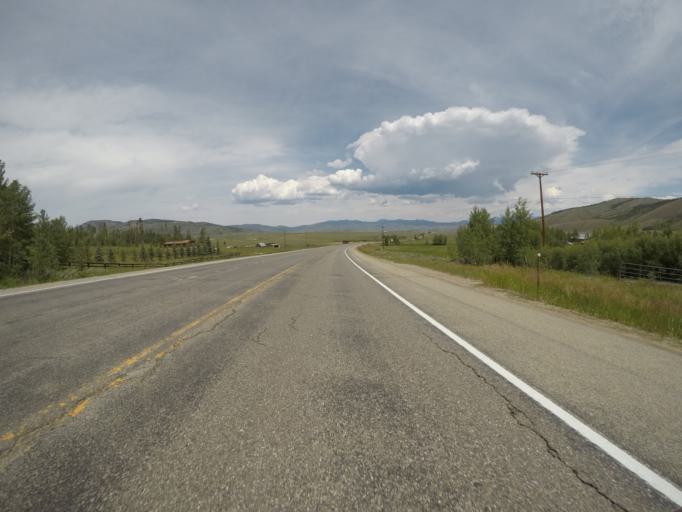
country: US
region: Colorado
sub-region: Grand County
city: Granby
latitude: 40.0181
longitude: -105.9417
